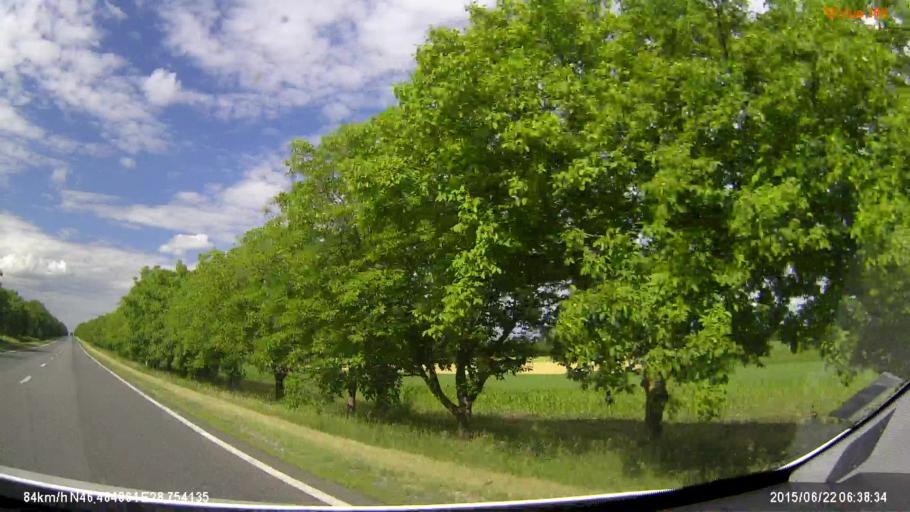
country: MD
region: Cimislia
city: Cimislia
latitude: 46.4845
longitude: 28.7540
